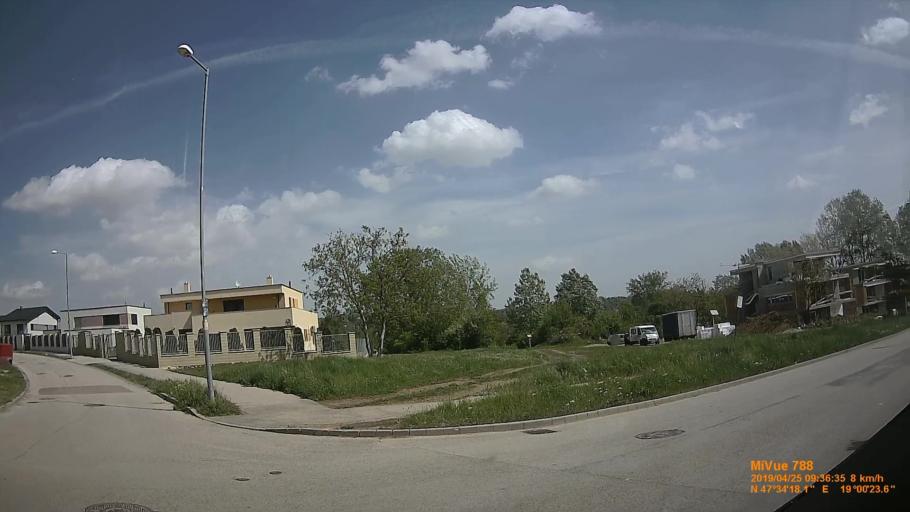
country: HU
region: Pest
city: Urom
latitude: 47.5723
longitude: 19.0073
